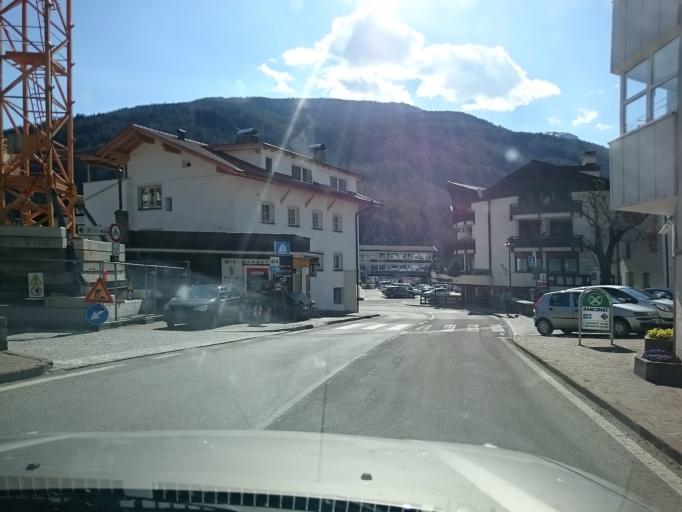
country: IT
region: Trentino-Alto Adige
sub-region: Bolzano
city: Brennero - Brenner
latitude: 46.9384
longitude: 11.4452
